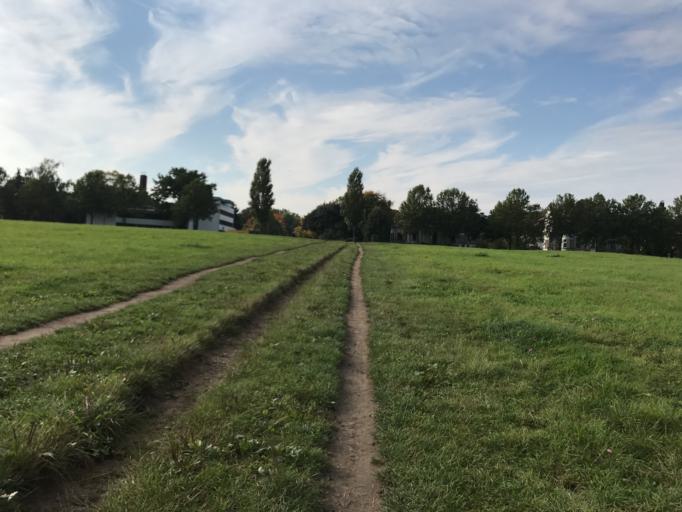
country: DE
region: Saxony
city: Albertstadt
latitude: 51.0605
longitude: 13.7932
